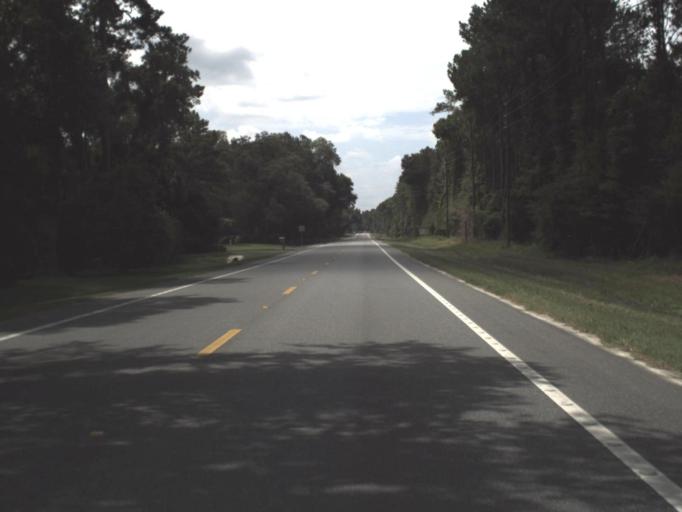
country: US
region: Florida
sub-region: Lafayette County
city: Mayo
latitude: 29.9736
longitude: -82.9332
